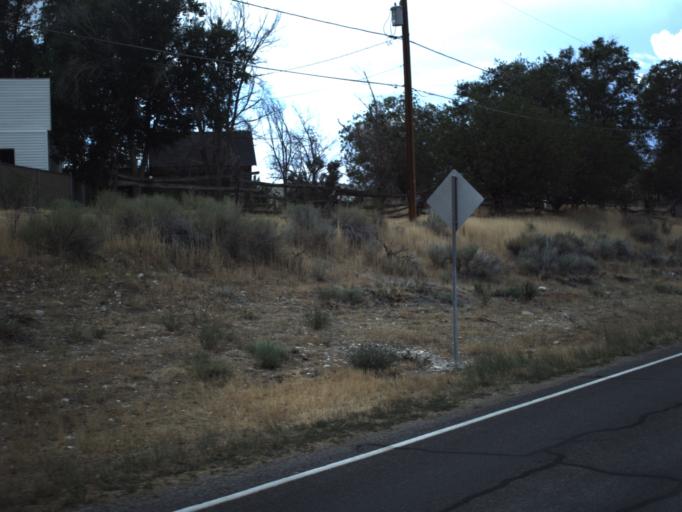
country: US
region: Utah
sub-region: Sanpete County
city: Centerfield
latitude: 39.1182
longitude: -111.7115
